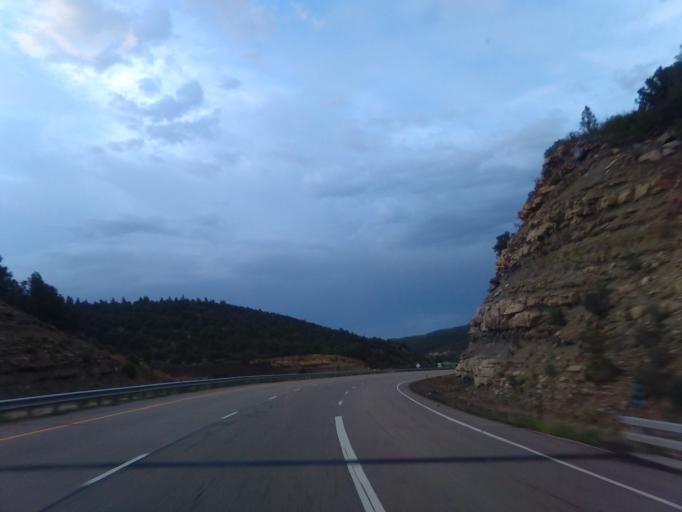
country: US
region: Colorado
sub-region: Las Animas County
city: Trinidad
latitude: 37.0603
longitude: -104.5231
